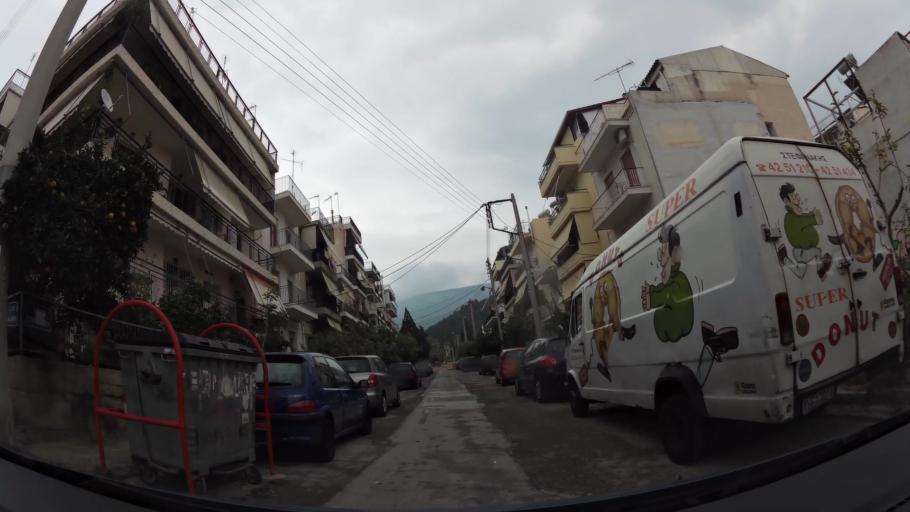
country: GR
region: Attica
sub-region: Nomarchia Athinas
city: Kaisariani
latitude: 37.9582
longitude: 23.7667
